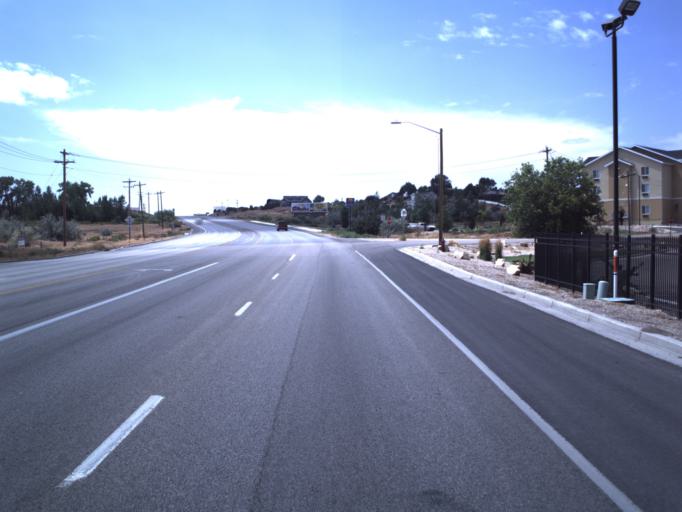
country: US
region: Utah
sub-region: Uintah County
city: Maeser
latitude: 40.4339
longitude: -109.5722
